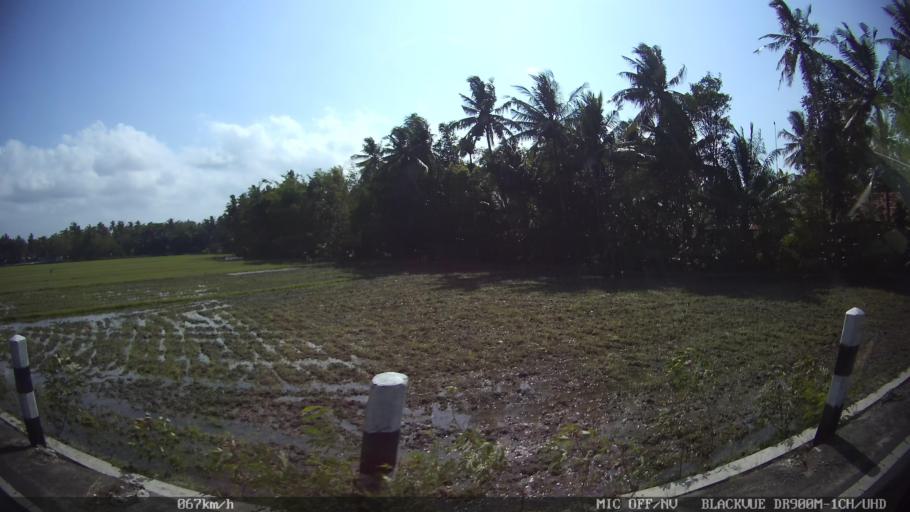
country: ID
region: Daerah Istimewa Yogyakarta
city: Srandakan
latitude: -7.9287
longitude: 110.1915
